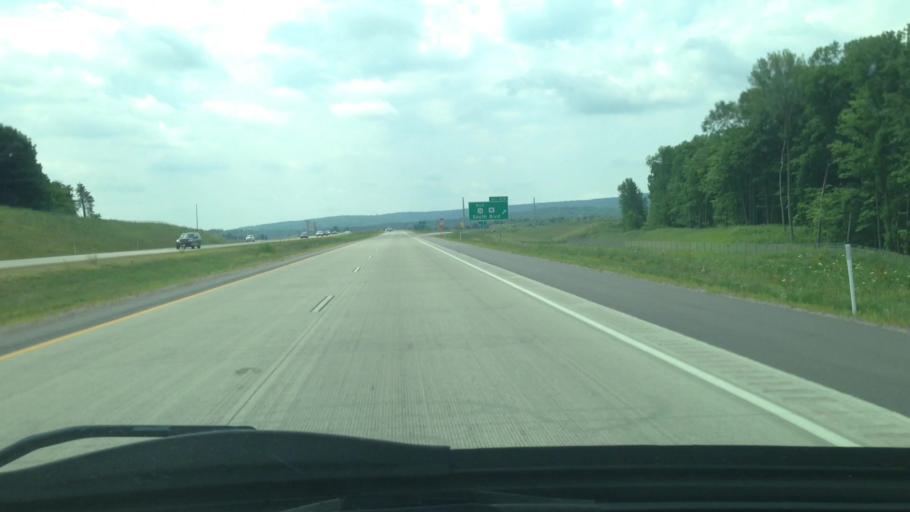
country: US
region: Wisconsin
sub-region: Sauk County
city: West Baraboo
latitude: 43.4662
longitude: -89.7772
